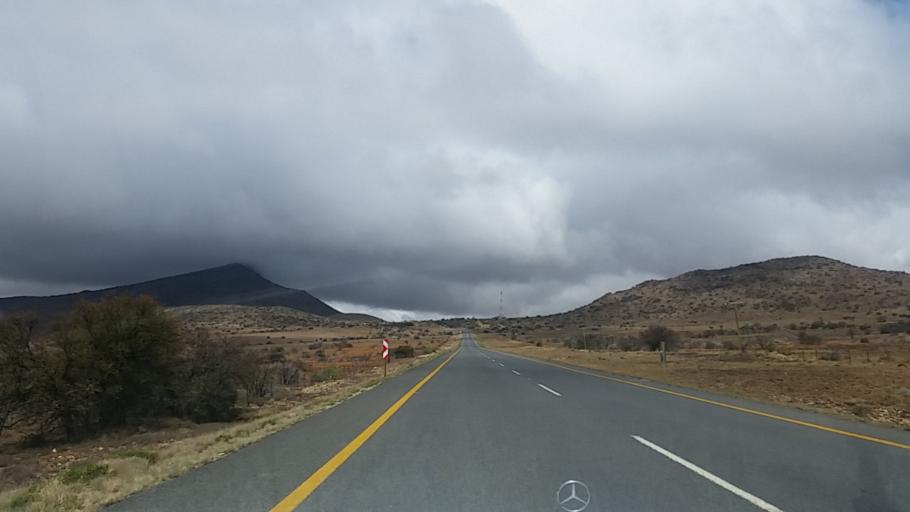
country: ZA
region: Eastern Cape
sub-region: Cacadu District Municipality
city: Graaff-Reinet
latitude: -32.0977
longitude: 24.6049
